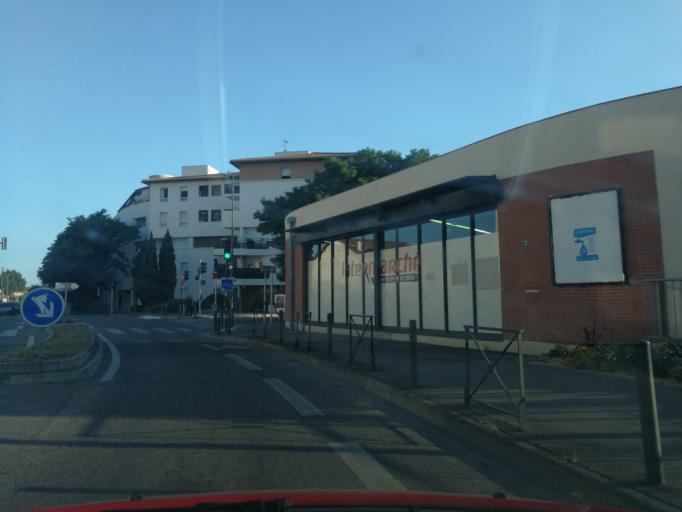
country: FR
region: Midi-Pyrenees
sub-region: Departement de la Haute-Garonne
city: Toulouse
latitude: 43.6249
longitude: 1.4547
